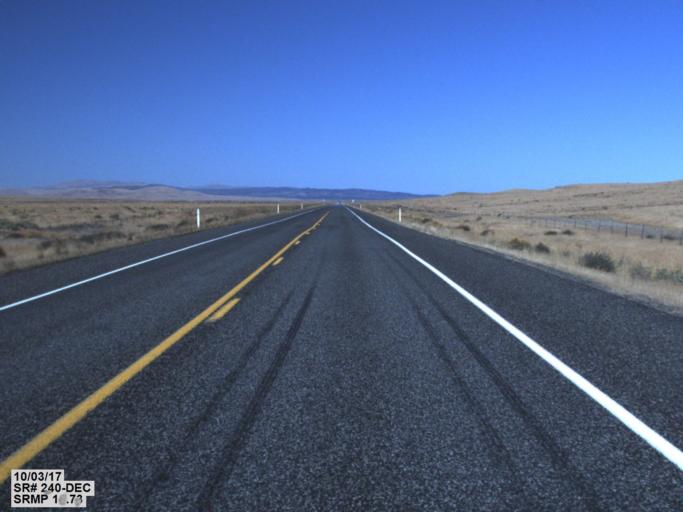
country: US
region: Washington
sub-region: Benton County
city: Benton City
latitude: 46.4471
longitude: -119.4990
